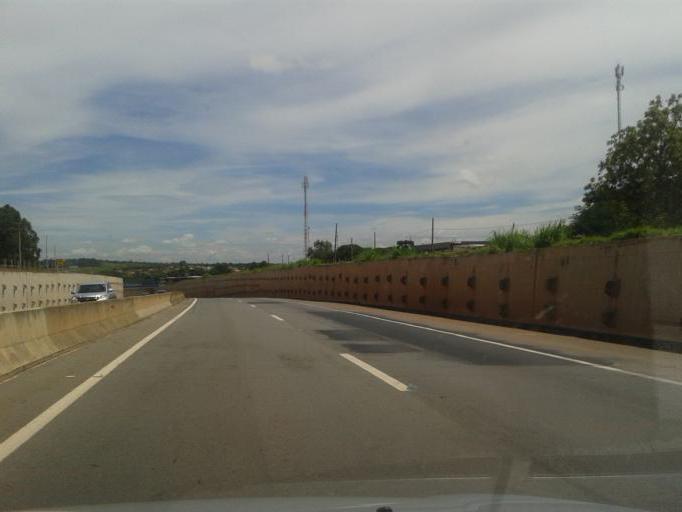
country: BR
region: Goias
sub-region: Hidrolandia
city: Hidrolandia
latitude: -16.9709
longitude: -49.2315
